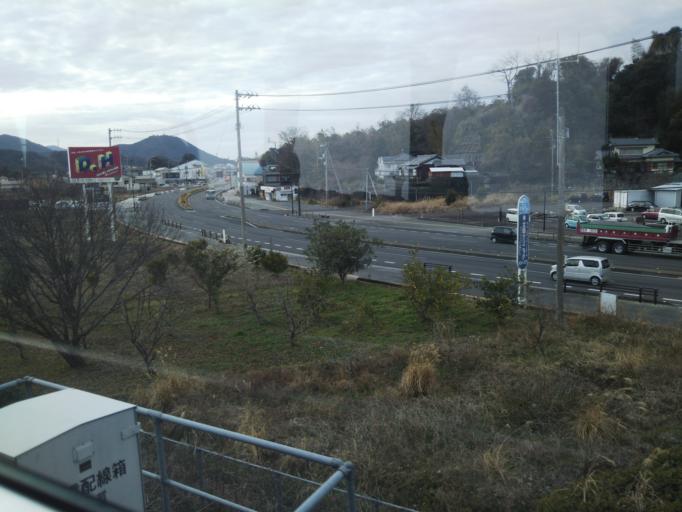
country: JP
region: Kochi
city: Nakamura
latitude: 32.9859
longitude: 132.9620
